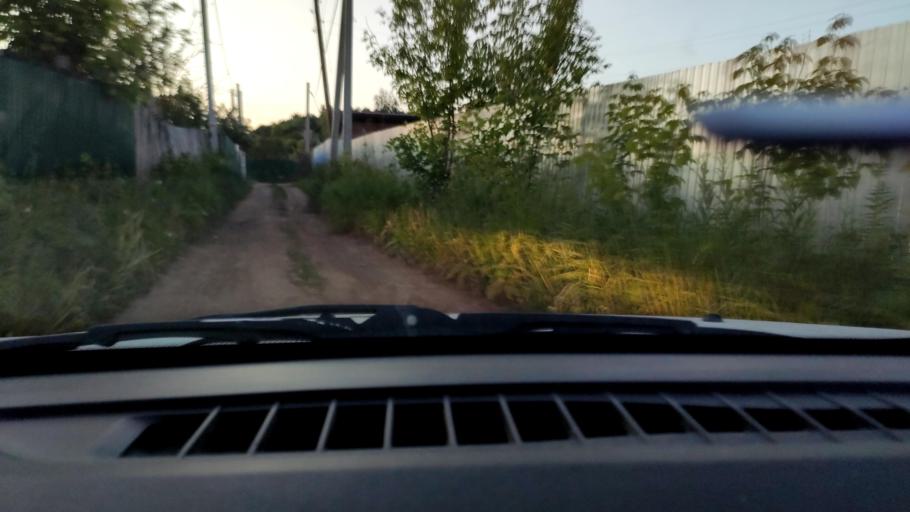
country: RU
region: Perm
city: Kondratovo
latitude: 57.9529
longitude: 56.1454
